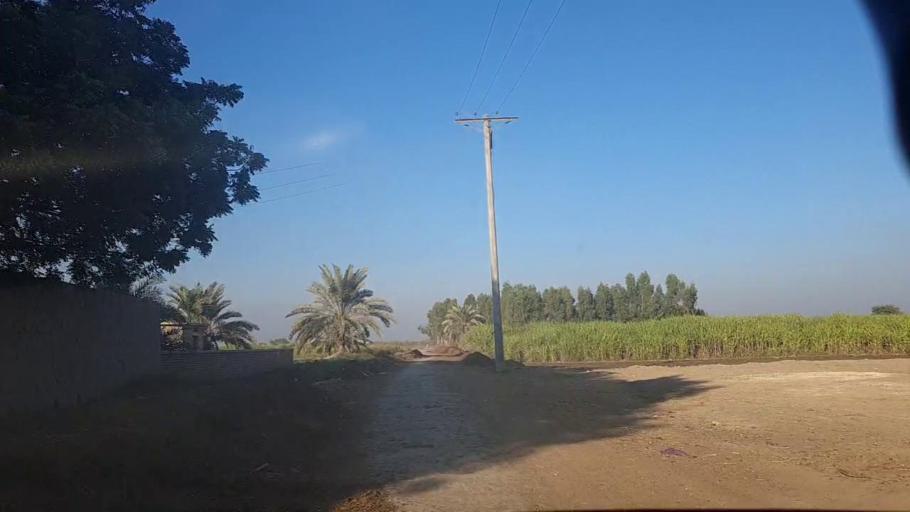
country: PK
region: Sindh
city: Sobhadero
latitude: 27.4011
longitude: 68.4209
